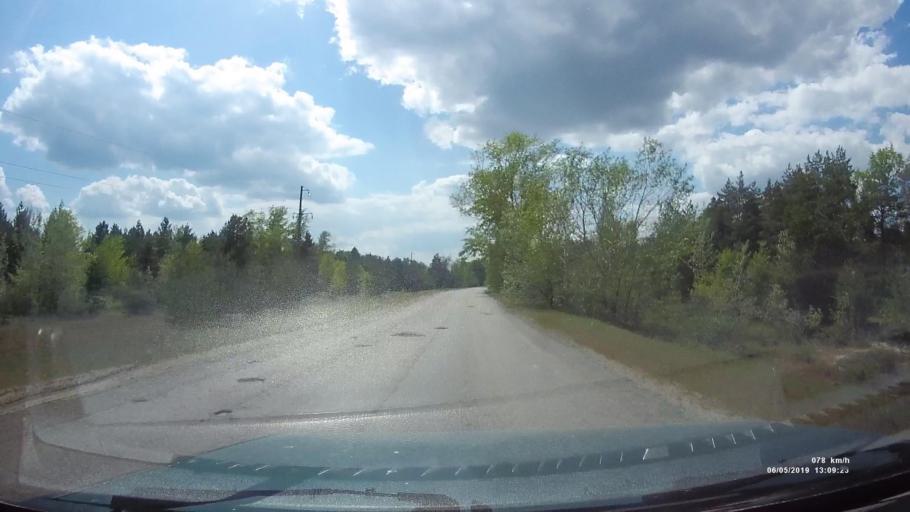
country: RU
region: Rostov
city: Ust'-Donetskiy
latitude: 47.7688
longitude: 40.9846
